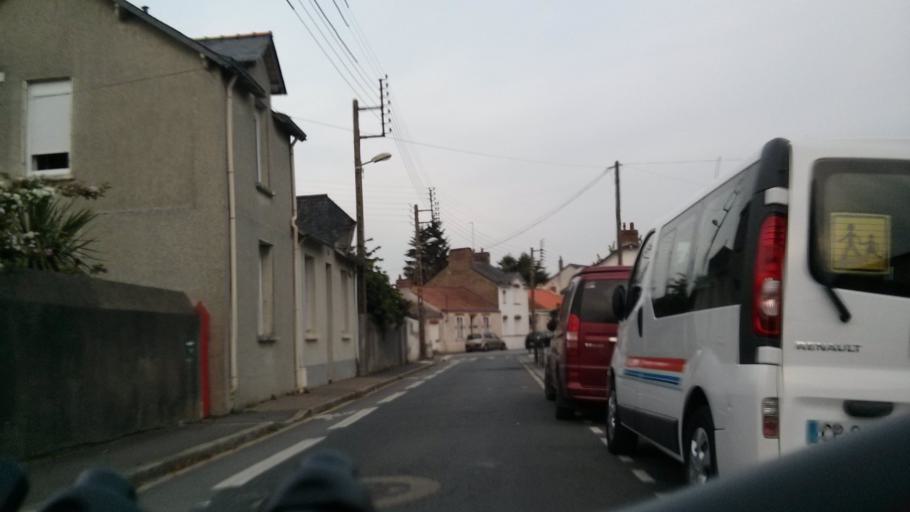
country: FR
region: Pays de la Loire
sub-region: Departement de la Loire-Atlantique
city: Reze
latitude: 47.1933
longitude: -1.5368
